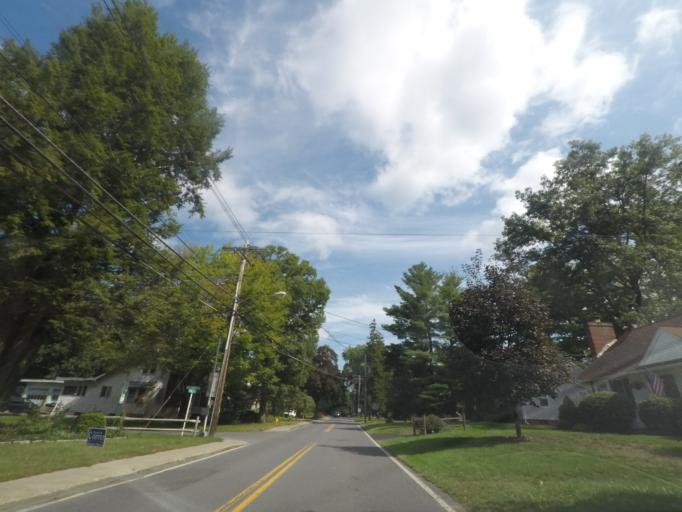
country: US
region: New York
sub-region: Albany County
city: Delmar
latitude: 42.6214
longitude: -73.8244
